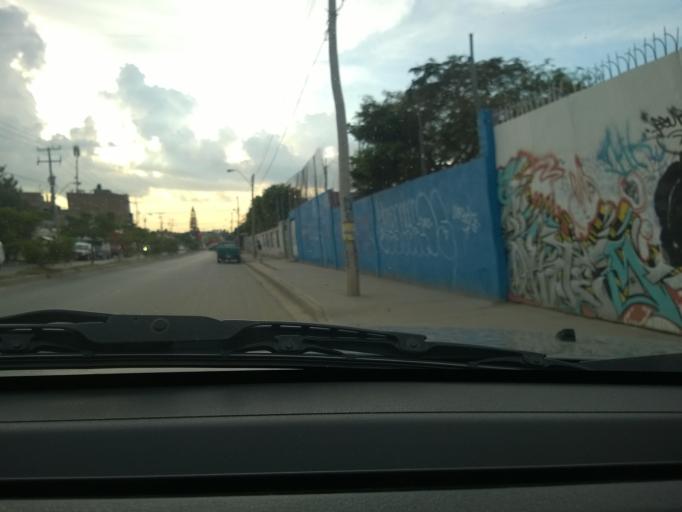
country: MX
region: Guanajuato
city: Leon
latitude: 21.1375
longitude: -101.6474
